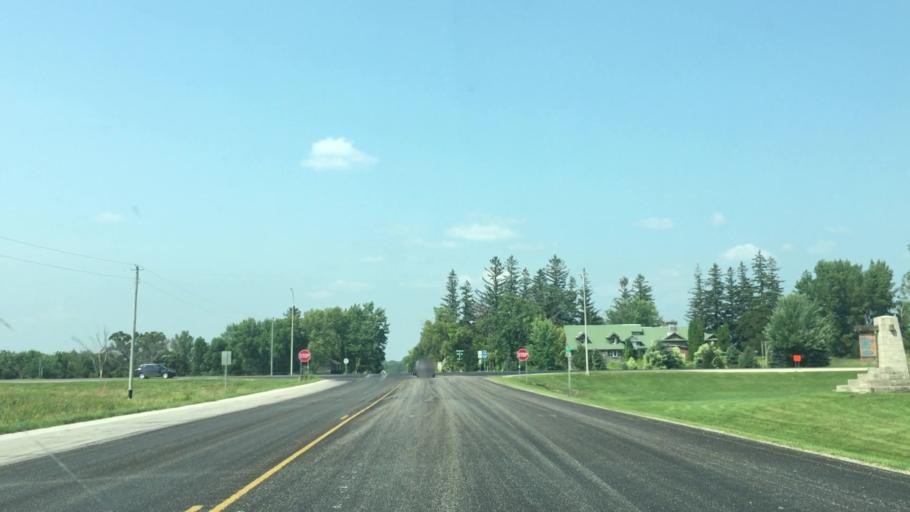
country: US
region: Minnesota
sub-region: Fillmore County
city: Harmony
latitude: 43.5140
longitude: -91.8697
